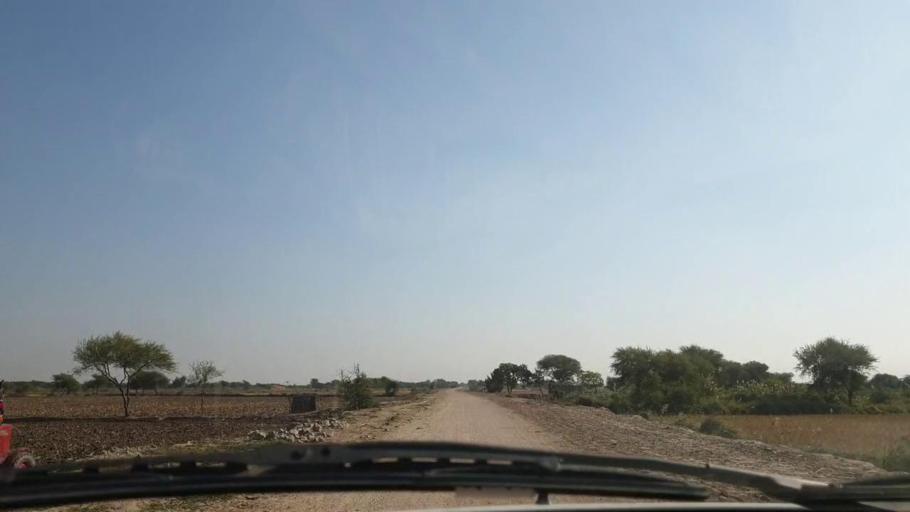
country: PK
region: Sindh
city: Bulri
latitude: 24.8015
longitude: 68.3930
